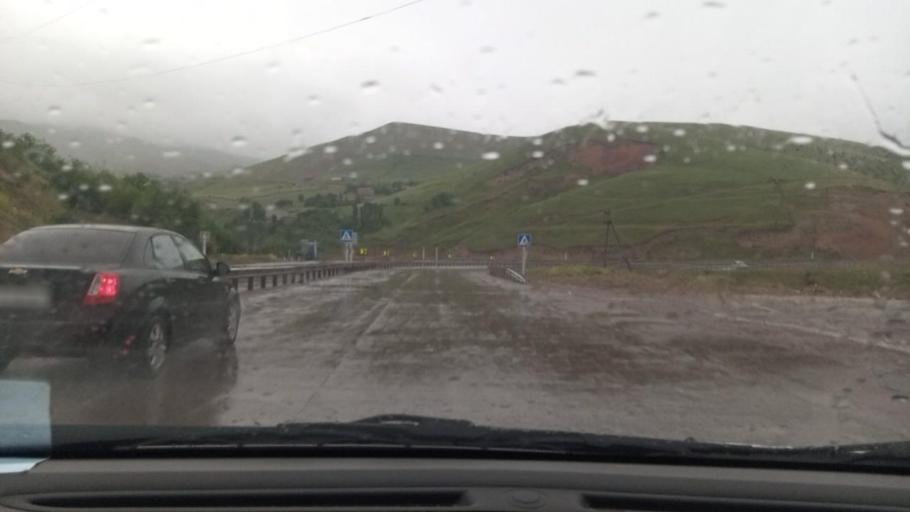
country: UZ
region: Toshkent
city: Angren
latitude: 41.0665
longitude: 70.2198
